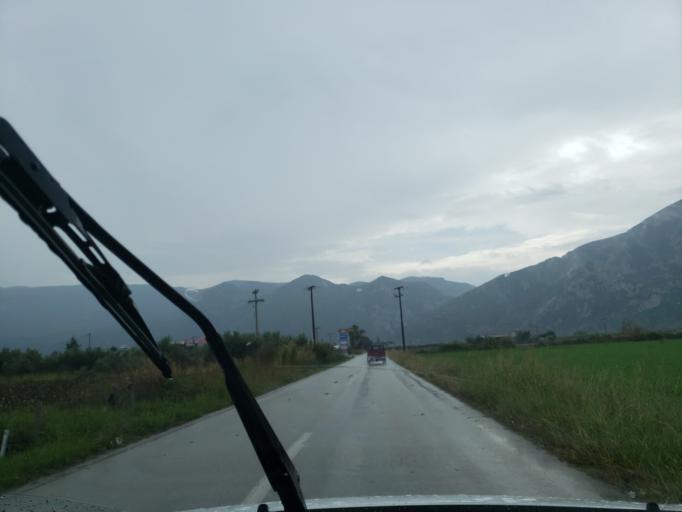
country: GR
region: Central Greece
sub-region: Nomos Fthiotidos
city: Anthili
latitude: 38.8133
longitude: 22.4423
